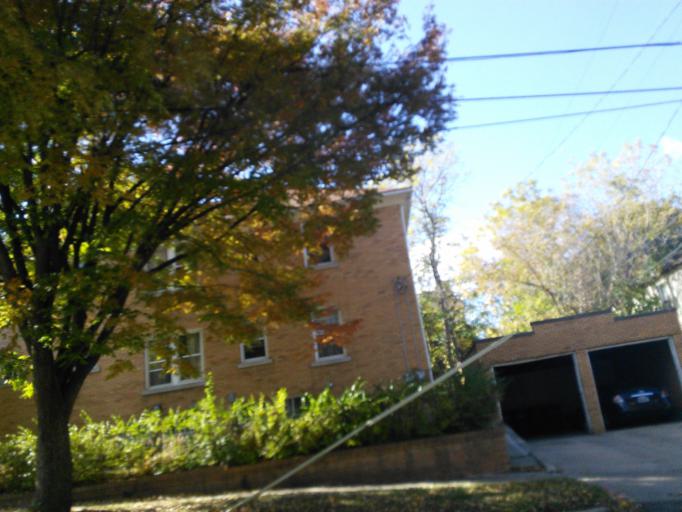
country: US
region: Michigan
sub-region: Washtenaw County
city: Ann Arbor
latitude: 42.2820
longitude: -83.7588
